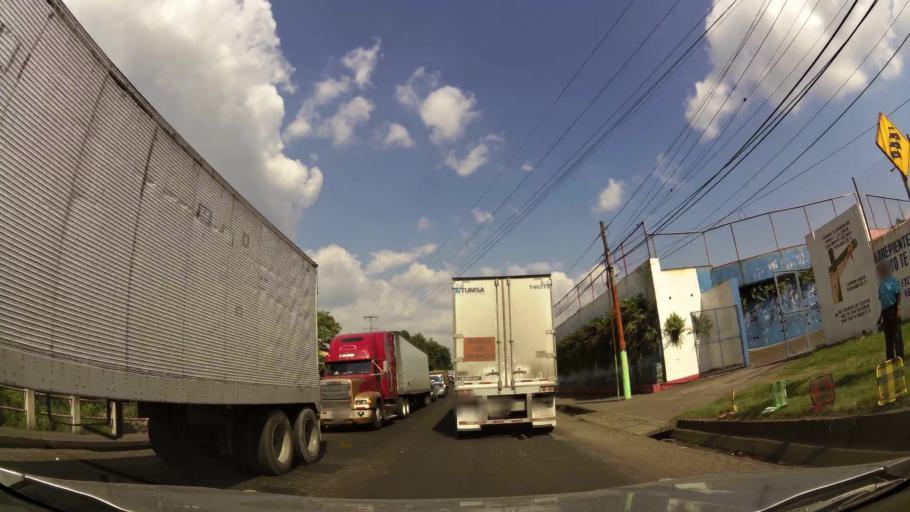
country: GT
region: Suchitepeque
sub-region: Municipio de Cuyotenango
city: Cuyotenango
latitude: 14.5417
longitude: -91.5700
